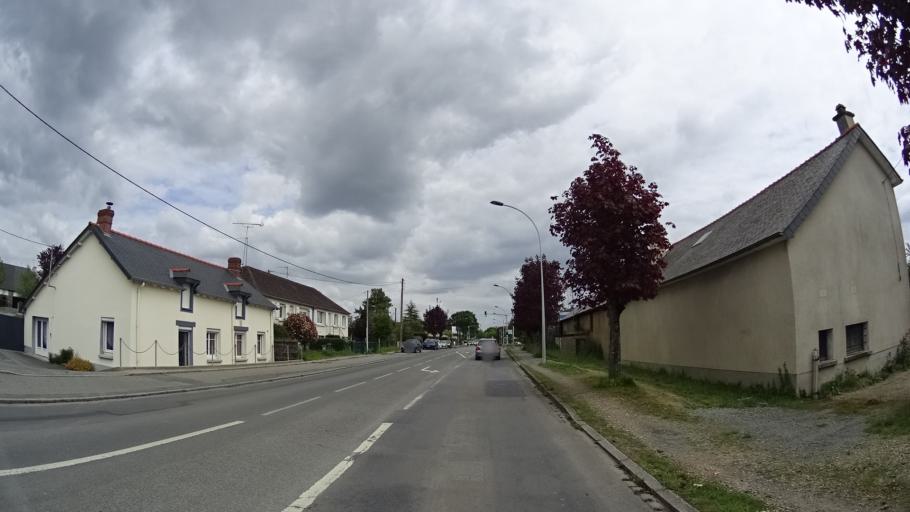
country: FR
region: Brittany
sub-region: Departement d'Ille-et-Vilaine
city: Mordelles
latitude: 48.0770
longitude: -1.8397
